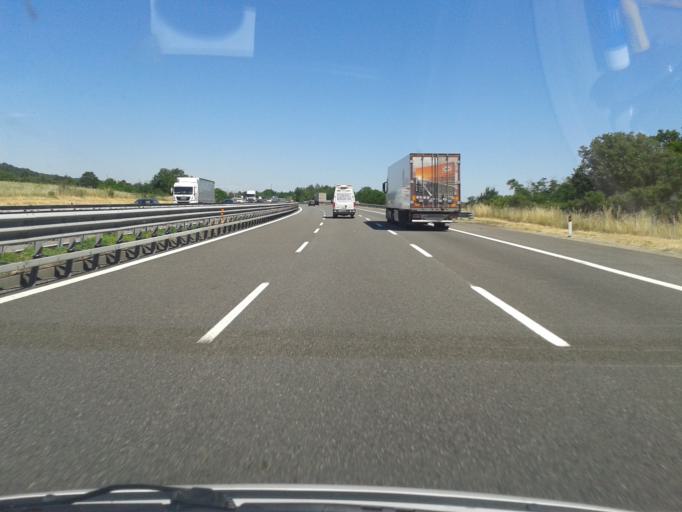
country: IT
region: Piedmont
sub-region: Provincia di Alessandria
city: Capriata d'Orba
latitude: 44.7237
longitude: 8.6671
